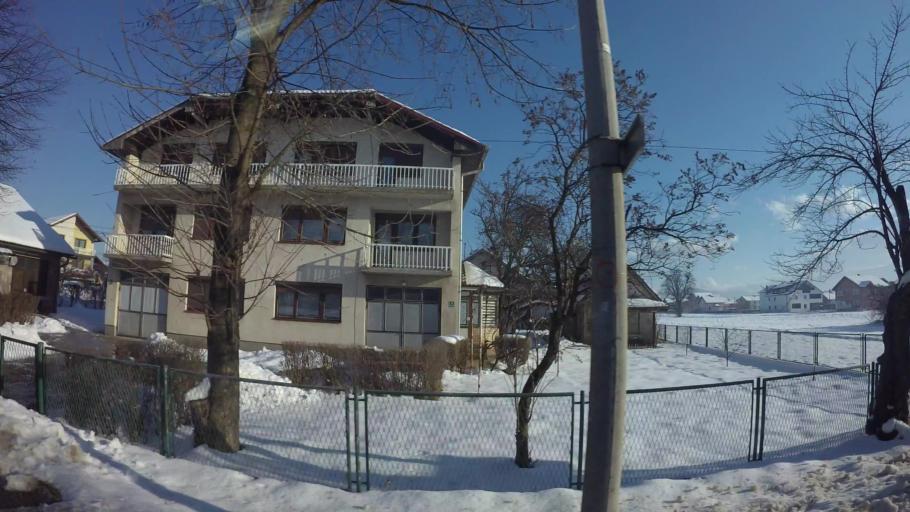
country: BA
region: Federation of Bosnia and Herzegovina
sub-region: Kanton Sarajevo
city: Sarajevo
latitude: 43.8191
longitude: 18.3306
